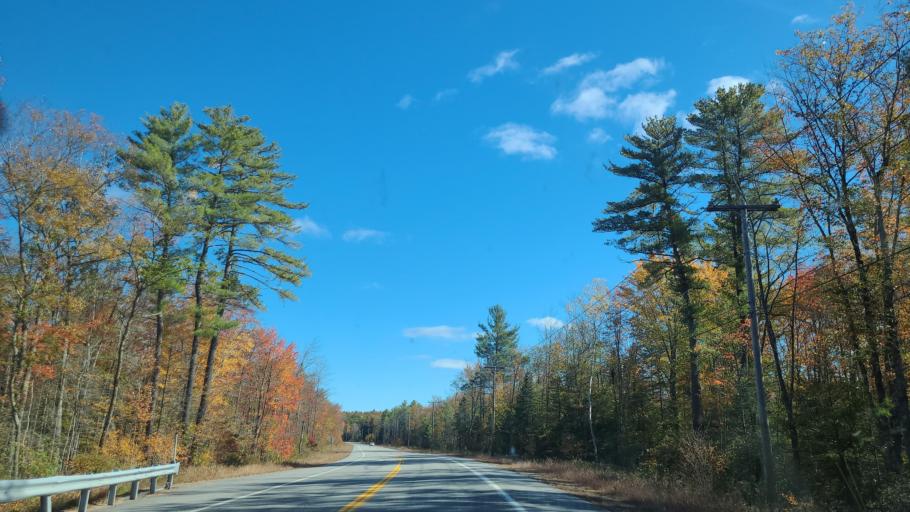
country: US
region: Maine
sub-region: Oxford County
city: Fryeburg
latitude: 44.0324
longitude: -70.8972
